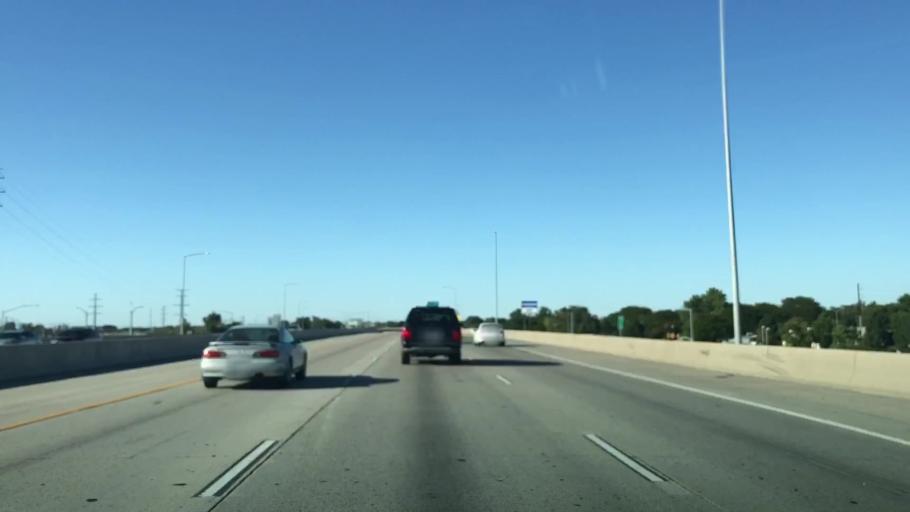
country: US
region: Colorado
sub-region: Adams County
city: Aurora
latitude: 39.7386
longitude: -104.8252
